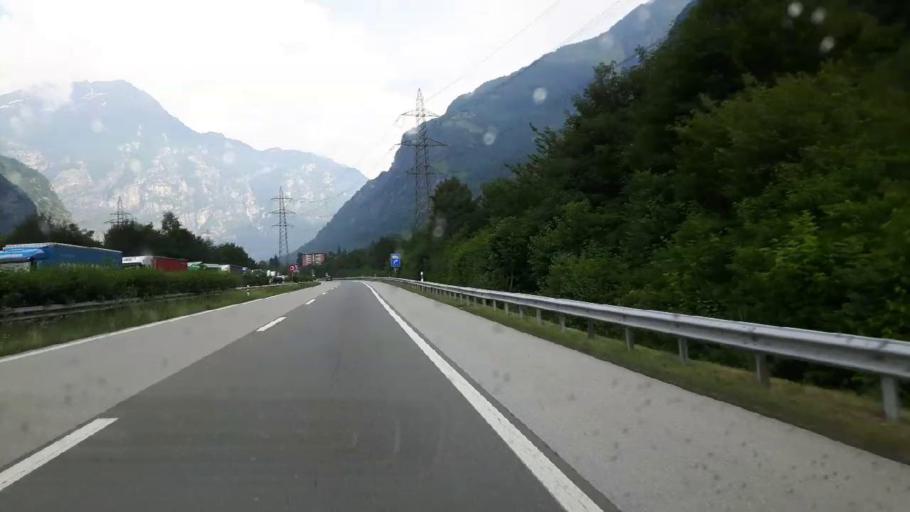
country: CH
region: Ticino
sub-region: Leventina District
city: Bodio
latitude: 46.3777
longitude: 8.9058
